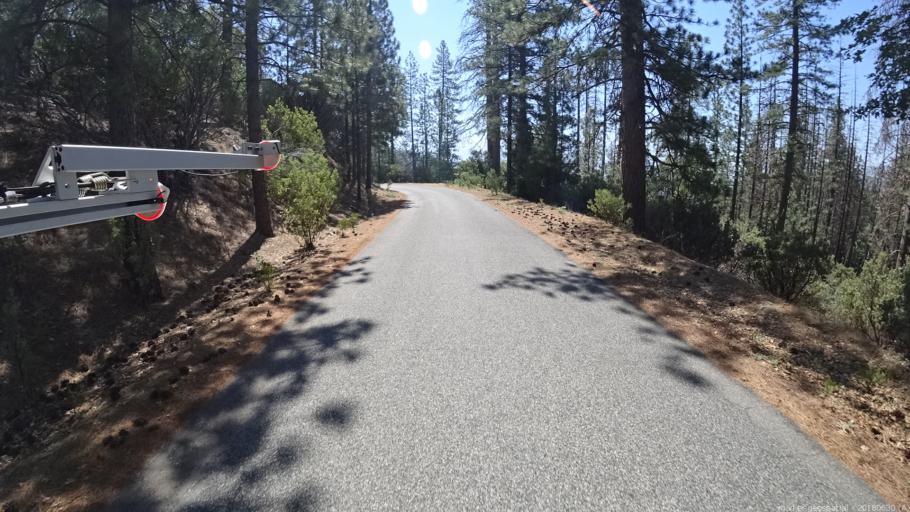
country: US
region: California
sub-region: Madera County
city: Oakhurst
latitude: 37.3800
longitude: -119.3603
